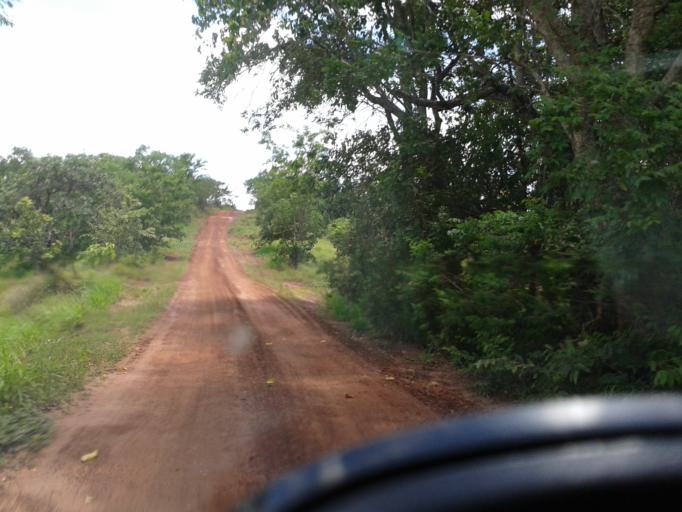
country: BR
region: Minas Gerais
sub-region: Santa Vitoria
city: Santa Vitoria
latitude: -18.9797
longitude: -49.8935
